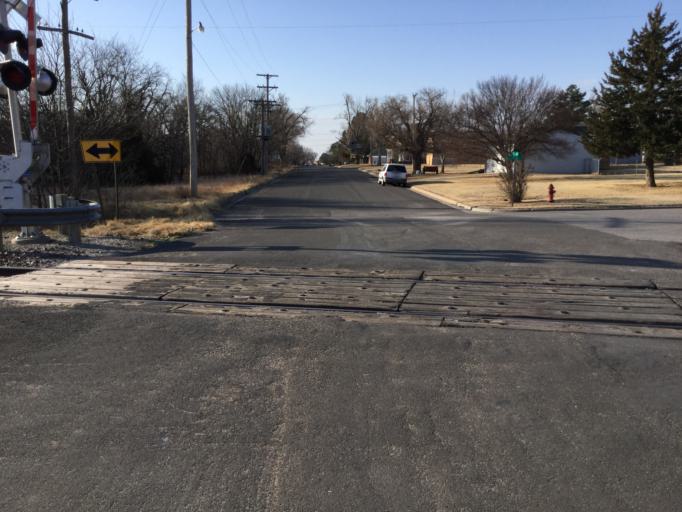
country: US
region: Kansas
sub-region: Rush County
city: La Crosse
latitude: 38.5300
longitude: -99.3013
